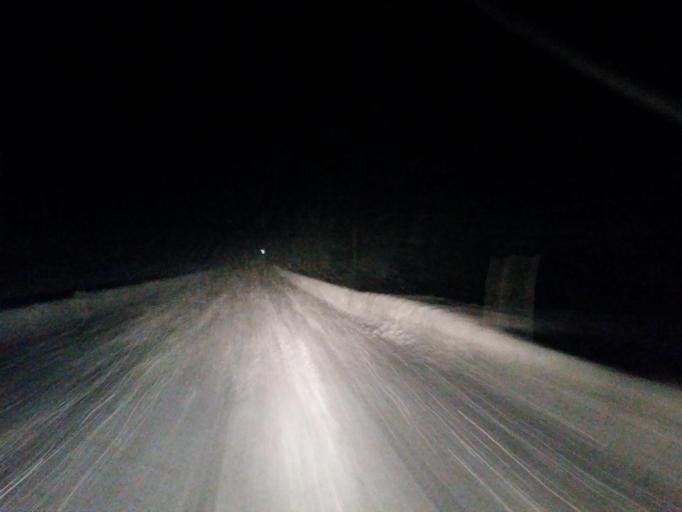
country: SE
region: Norrbotten
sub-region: Alvsbyns Kommun
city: AElvsbyn
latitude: 65.6273
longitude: 21.1137
